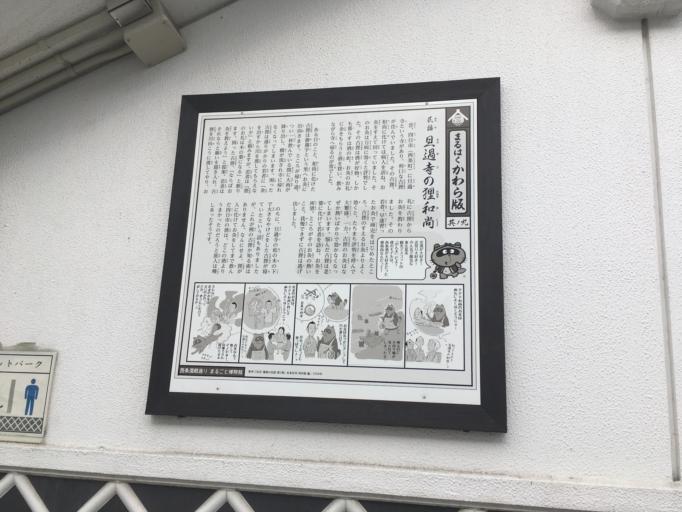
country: JP
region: Hiroshima
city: Takehara
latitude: 34.4304
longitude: 132.7449
